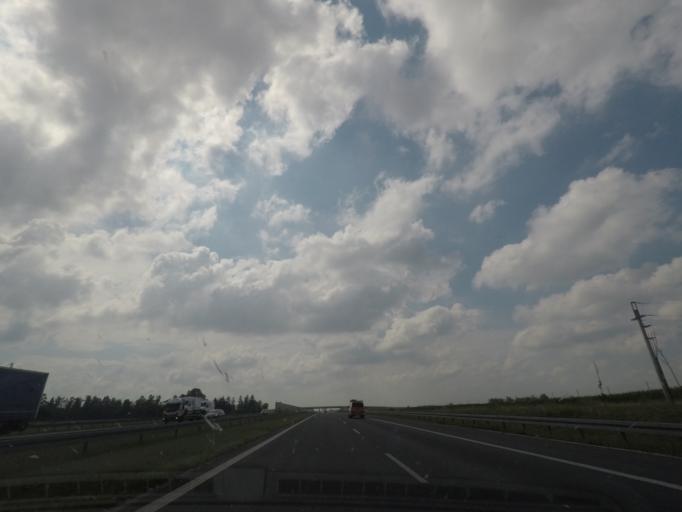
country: PL
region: Lodz Voivodeship
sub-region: Powiat kutnowski
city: Krzyzanow
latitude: 52.1614
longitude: 19.4833
